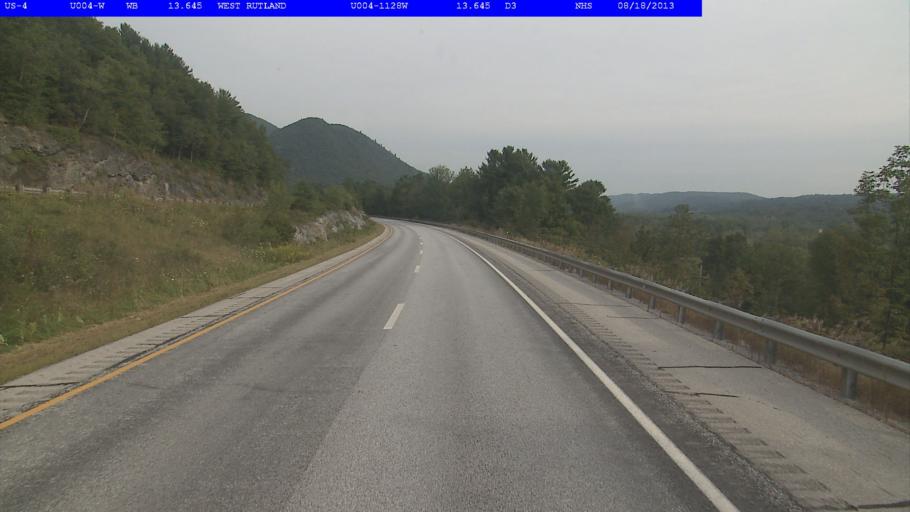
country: US
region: Vermont
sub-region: Rutland County
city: West Rutland
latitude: 43.5977
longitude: -73.0571
